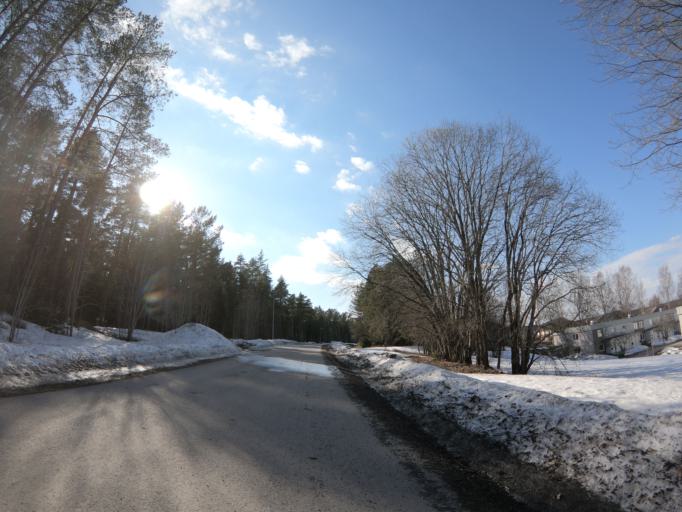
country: SE
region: Vaesterbotten
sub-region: Umea Kommun
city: Ersmark
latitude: 63.8430
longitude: 20.3100
